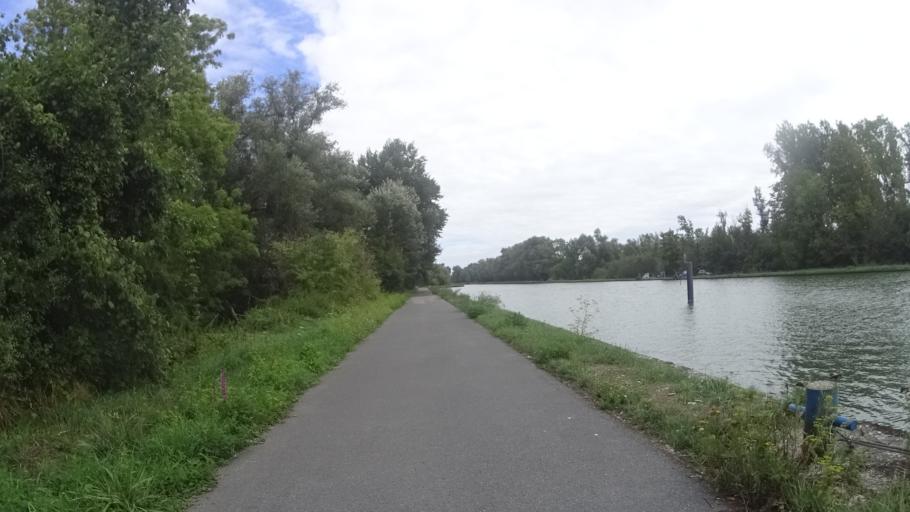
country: FR
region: Picardie
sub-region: Departement de l'Oise
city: Noyon
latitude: 49.5631
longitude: 3.0009
